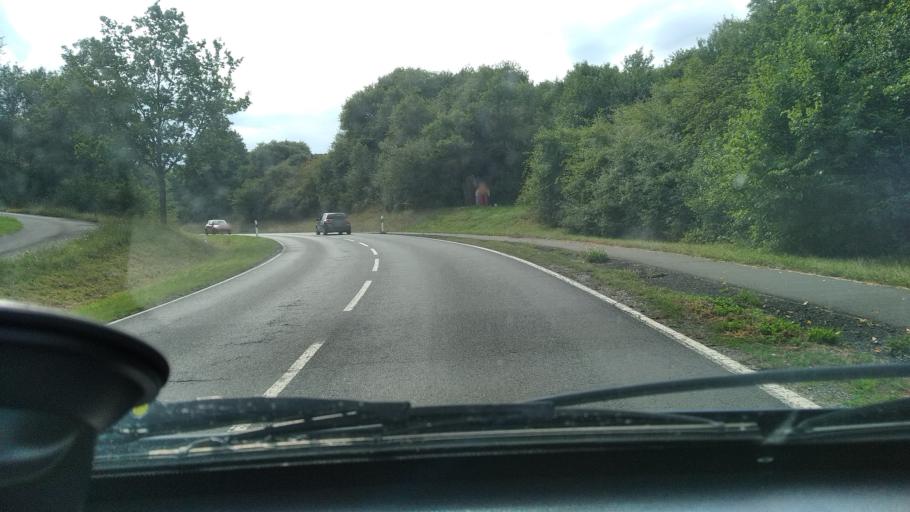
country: DE
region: Hesse
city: Dillenburg
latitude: 50.7419
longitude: 8.3140
